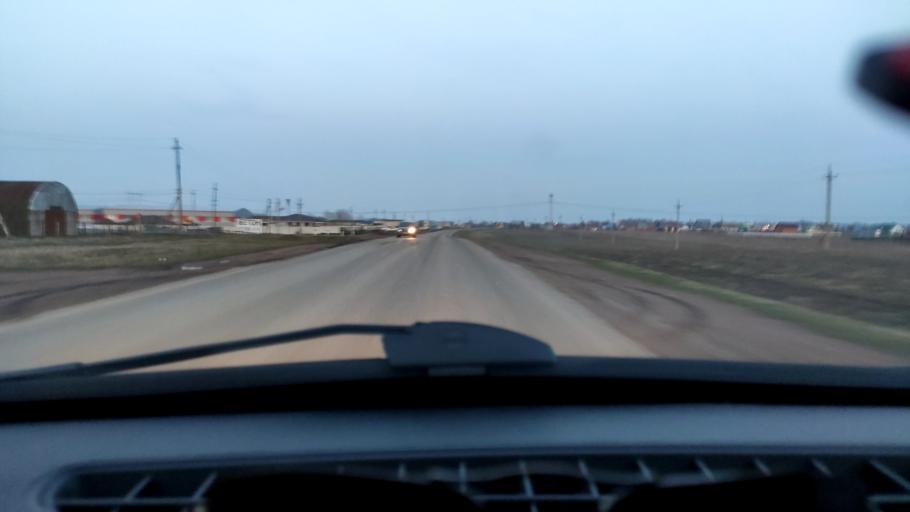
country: RU
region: Bashkortostan
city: Kabakovo
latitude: 54.5407
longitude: 56.1311
